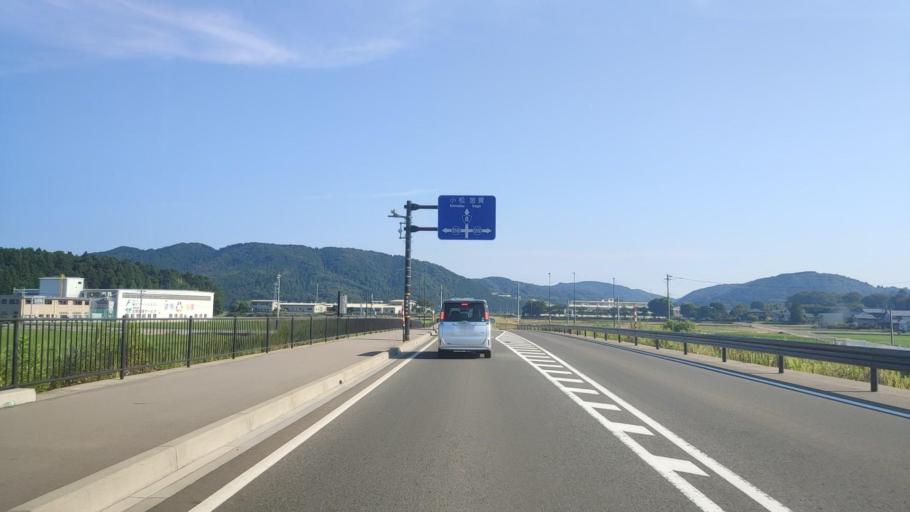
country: JP
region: Fukui
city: Maruoka
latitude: 36.1923
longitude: 136.2680
